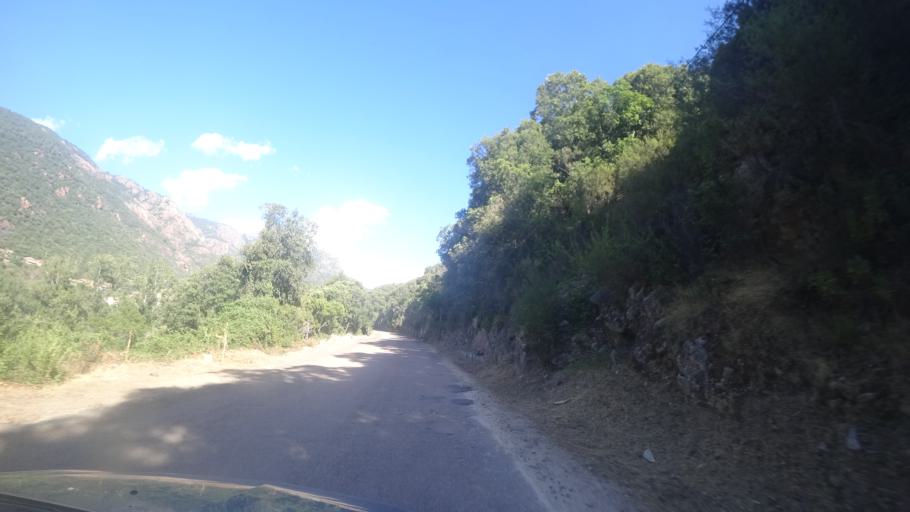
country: FR
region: Corsica
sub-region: Departement de la Corse-du-Sud
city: Cargese
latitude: 42.2633
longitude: 8.6977
